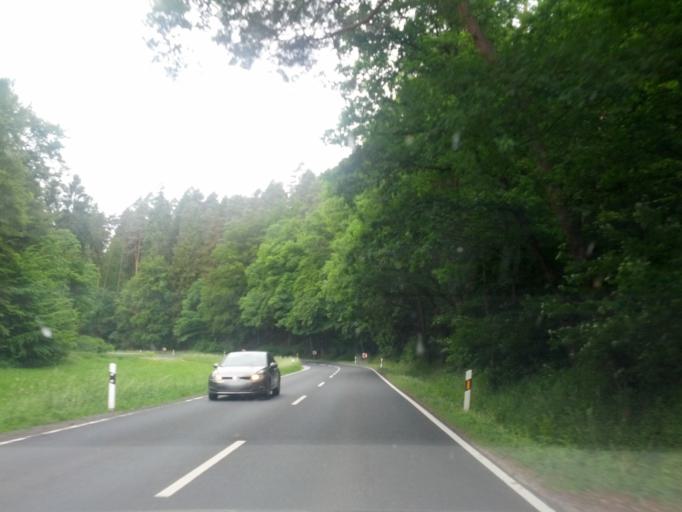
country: DE
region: Thuringia
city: Frauensee
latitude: 50.8639
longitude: 10.1531
